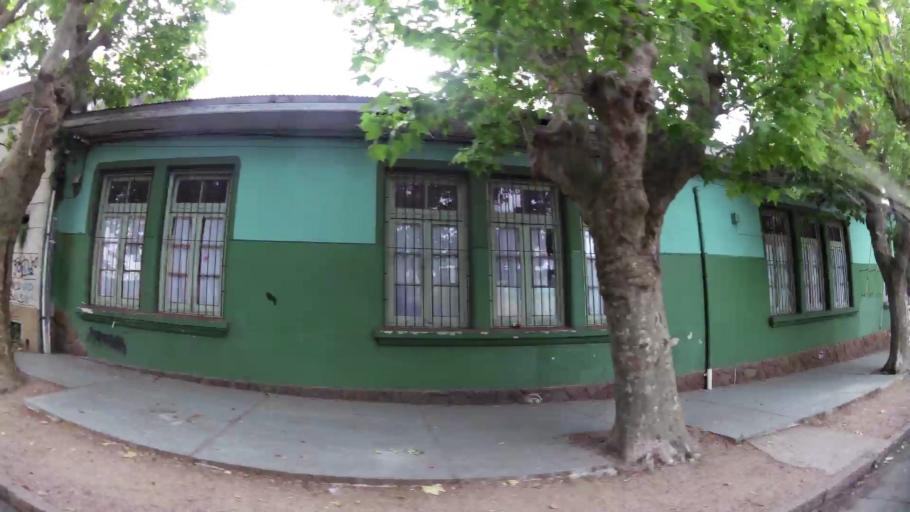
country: UY
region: Canelones
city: La Paz
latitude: -34.7635
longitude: -56.2248
